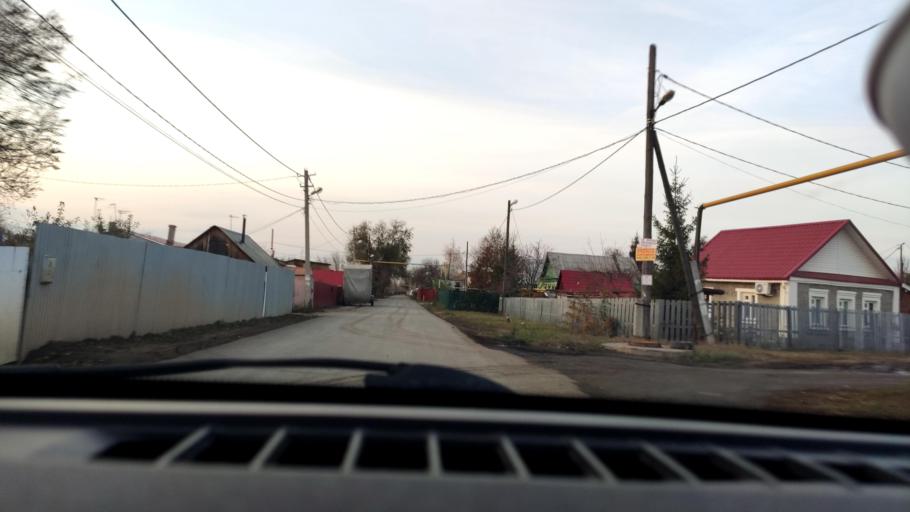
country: RU
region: Samara
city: Samara
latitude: 53.1387
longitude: 50.1359
